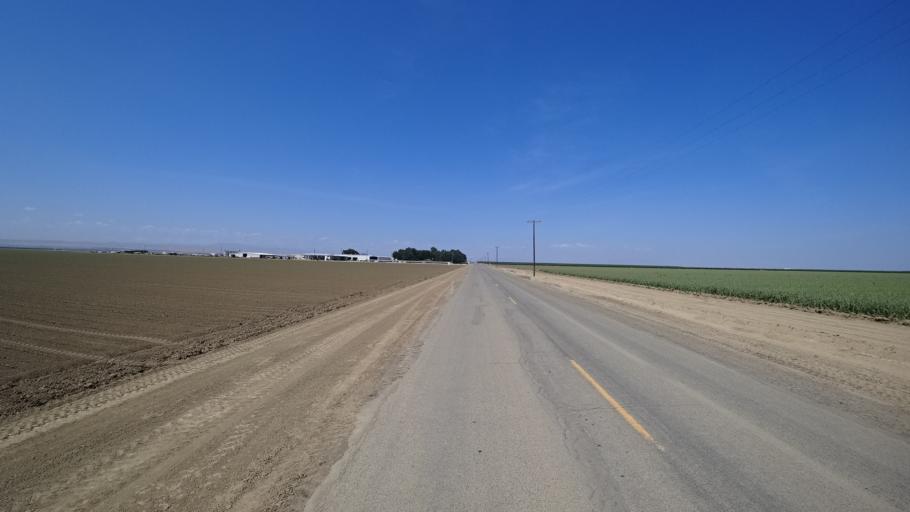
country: US
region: California
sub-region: Kings County
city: Kettleman City
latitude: 36.1377
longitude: -119.9804
